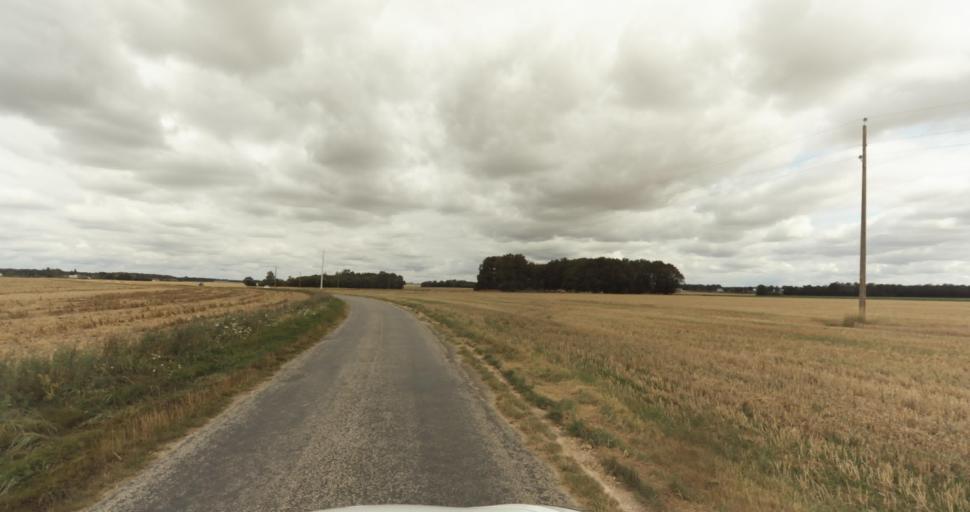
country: FR
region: Haute-Normandie
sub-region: Departement de l'Eure
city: Nonancourt
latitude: 48.7917
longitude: 1.1430
